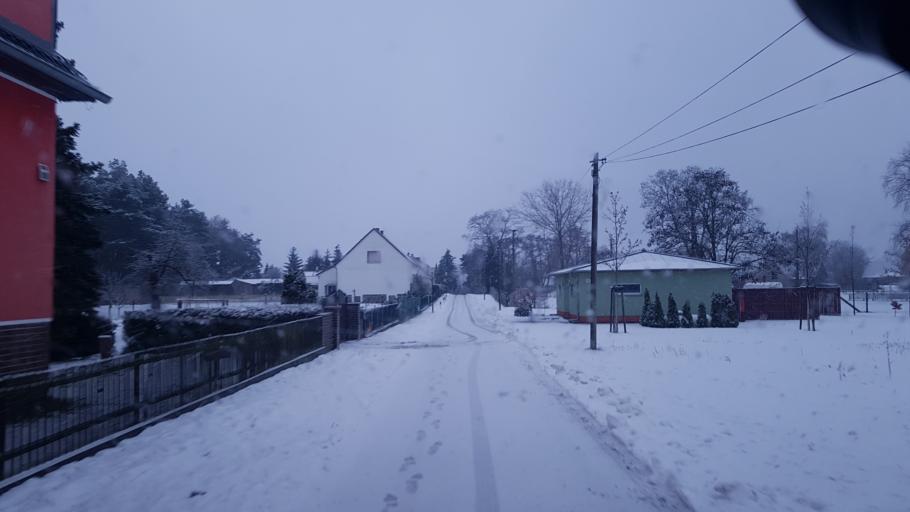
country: DE
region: Brandenburg
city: Janschwalde
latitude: 51.8977
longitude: 14.5201
